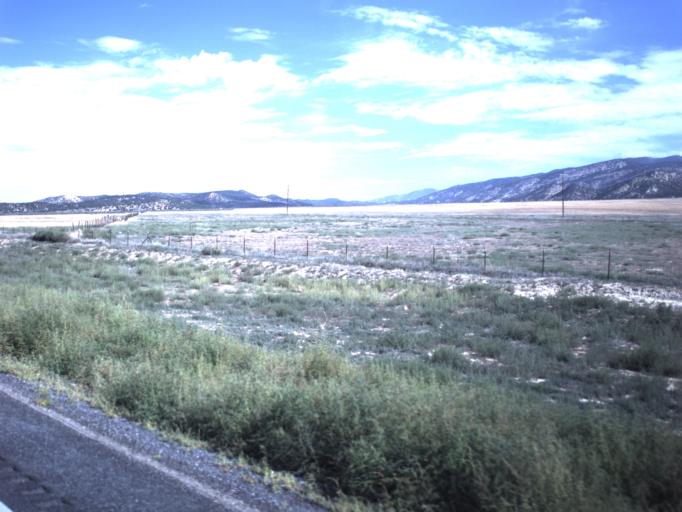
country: US
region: Utah
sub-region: Sanpete County
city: Gunnison
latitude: 39.3041
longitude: -111.8958
